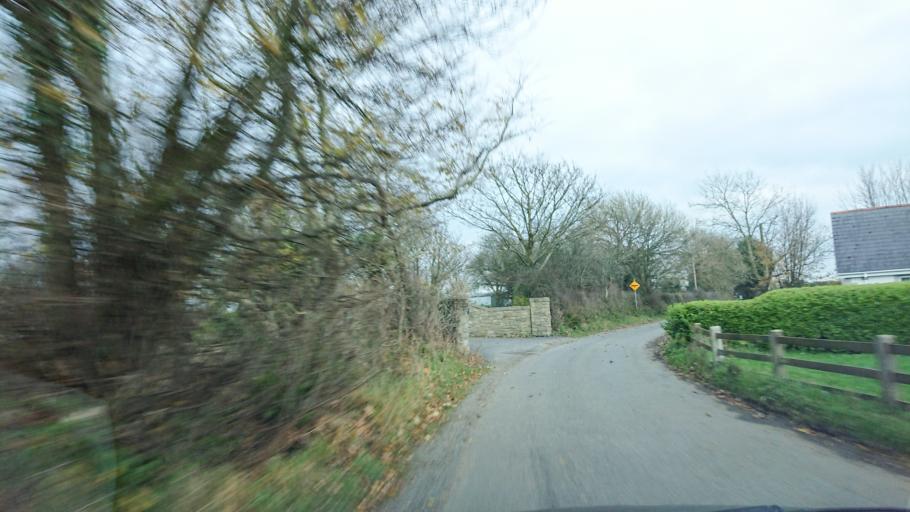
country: IE
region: Munster
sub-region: Waterford
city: Dunmore East
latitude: 52.2455
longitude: -6.9979
